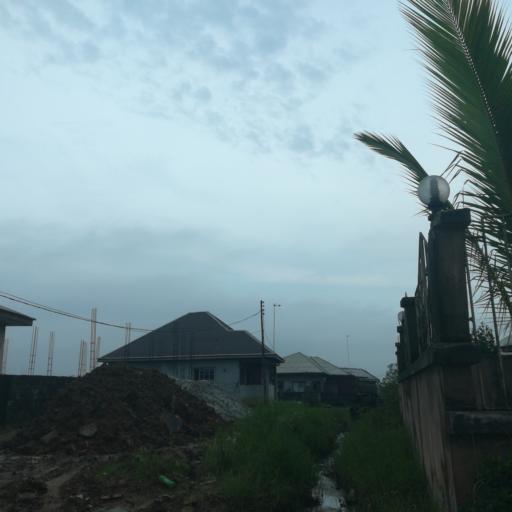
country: NG
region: Rivers
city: Port Harcourt
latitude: 4.7512
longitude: 7.0073
